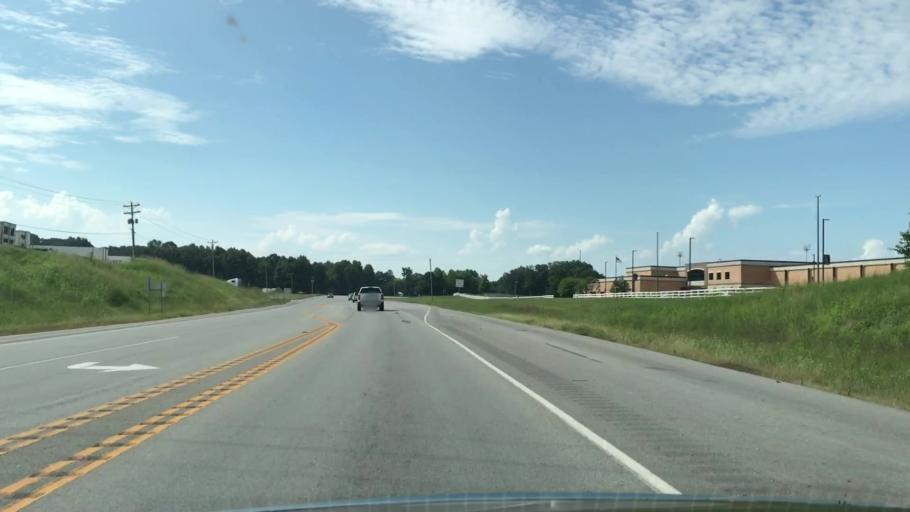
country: US
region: Kentucky
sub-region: Allen County
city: Scottsville
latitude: 36.7549
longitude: -86.2136
